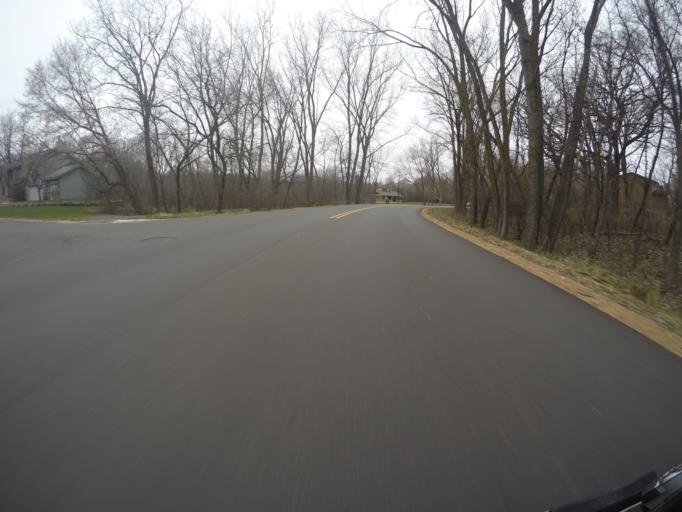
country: US
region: Minnesota
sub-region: Hennepin County
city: Eden Prairie
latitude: 44.8769
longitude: -93.4734
